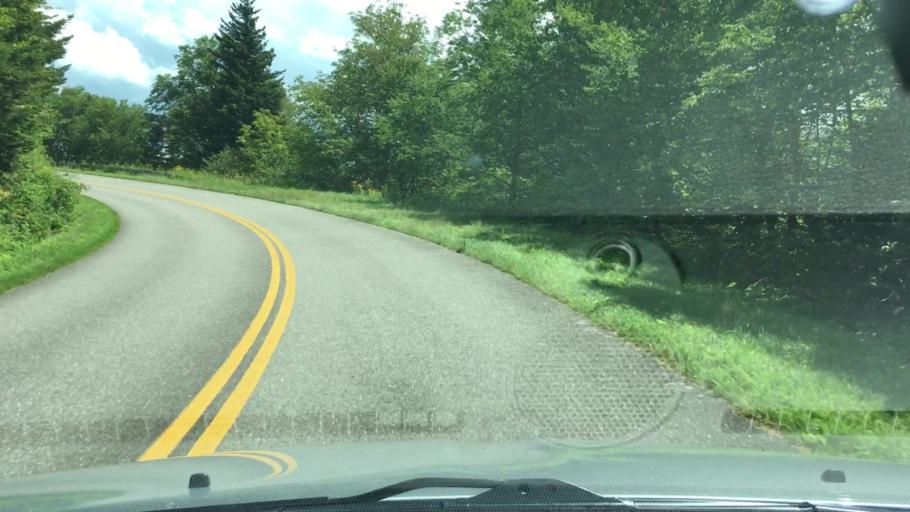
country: US
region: North Carolina
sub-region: Buncombe County
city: Black Mountain
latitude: 35.7357
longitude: -82.3229
